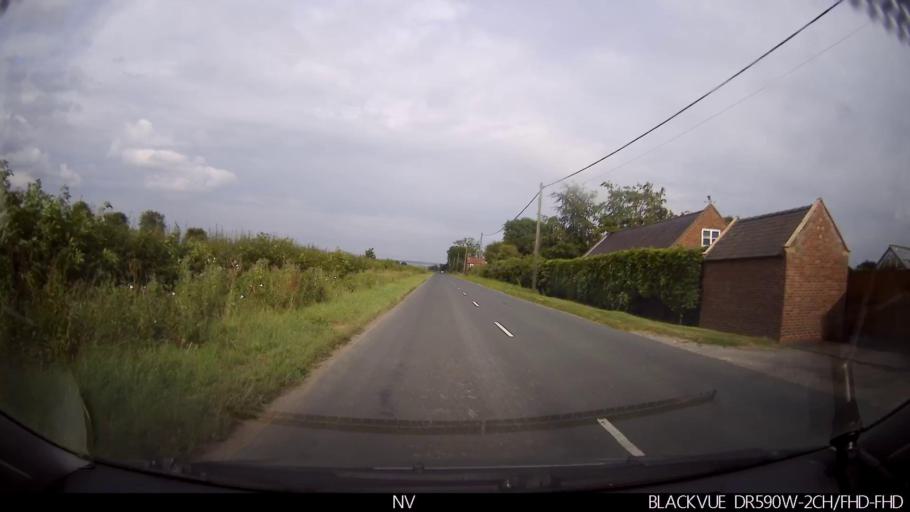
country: GB
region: England
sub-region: North Yorkshire
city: Marishes
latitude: 54.2071
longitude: -0.7915
